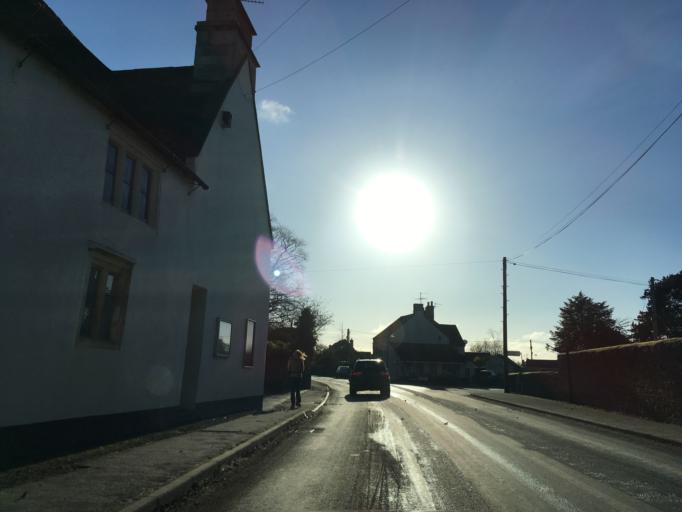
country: GB
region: England
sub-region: Wiltshire
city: Biddestone
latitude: 51.4869
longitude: -2.1935
